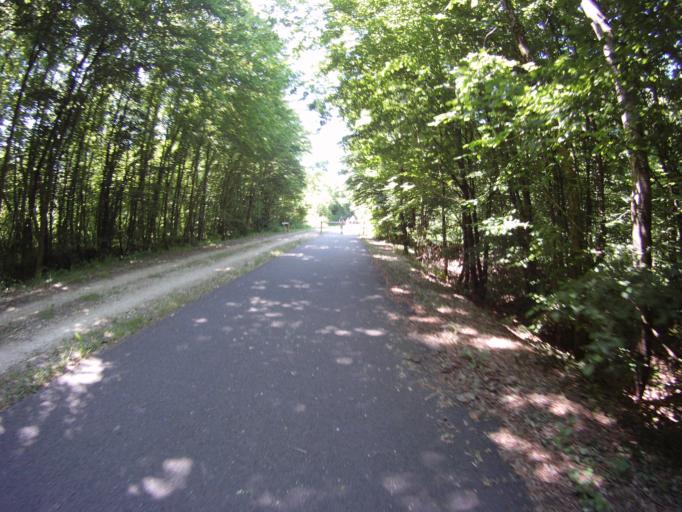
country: FR
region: Lorraine
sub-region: Departement de Meurthe-et-Moselle
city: Champenoux
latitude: 48.7554
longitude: 6.3308
